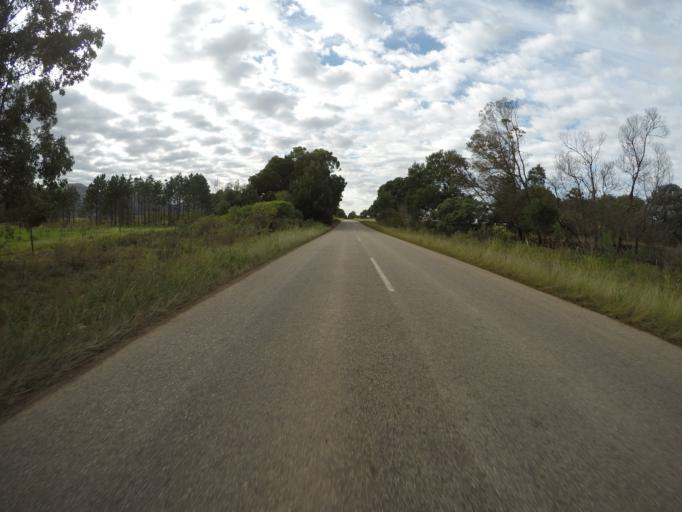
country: ZA
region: Eastern Cape
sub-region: Cacadu District Municipality
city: Kareedouw
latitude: -34.0442
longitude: 24.4341
